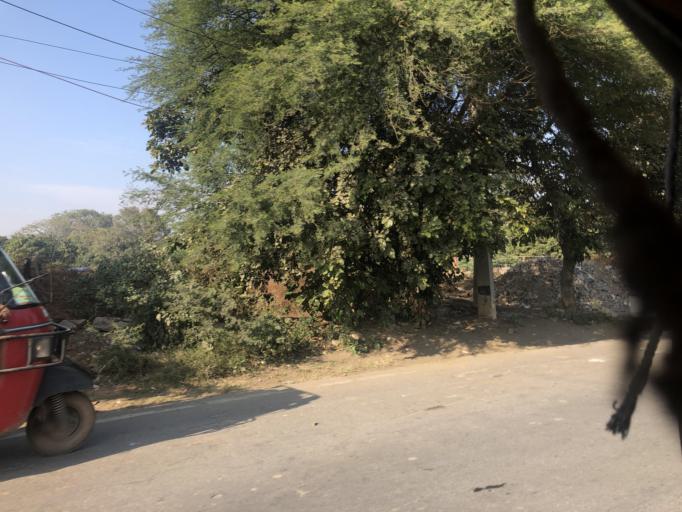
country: IN
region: Haryana
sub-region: Gurgaon
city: Gurgaon
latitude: 28.4631
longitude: 77.0700
